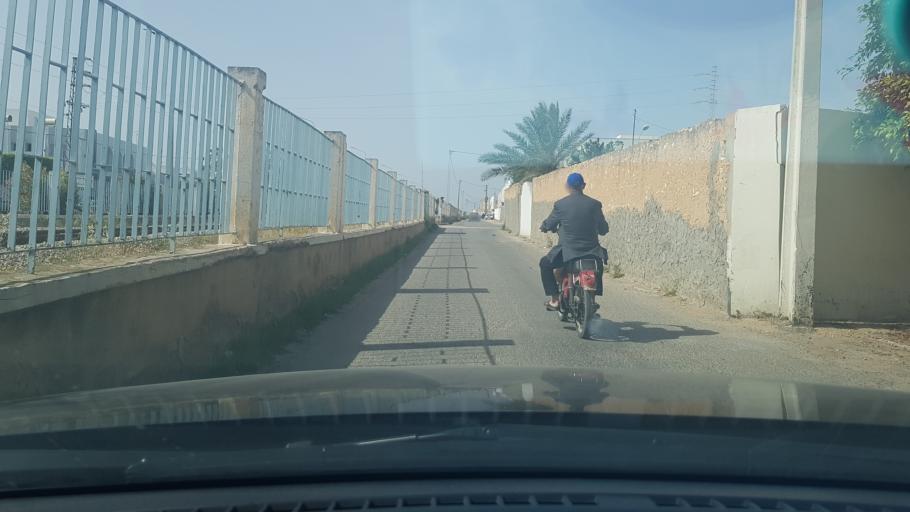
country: TN
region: Safaqis
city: Al Qarmadah
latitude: 34.8103
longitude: 10.7619
